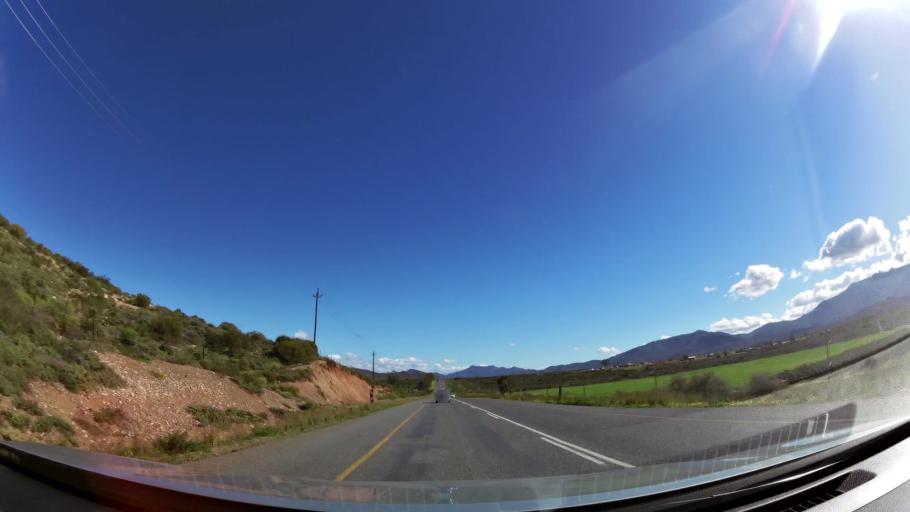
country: ZA
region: Western Cape
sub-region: Cape Winelands District Municipality
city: Ashton
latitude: -33.8142
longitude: 19.9322
